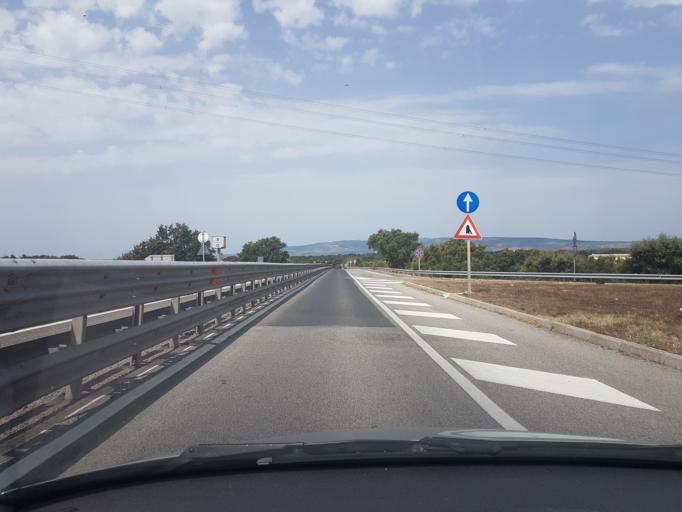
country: IT
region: Sardinia
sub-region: Provincia di Oristano
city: Abbasanta
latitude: 40.1139
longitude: 8.7973
